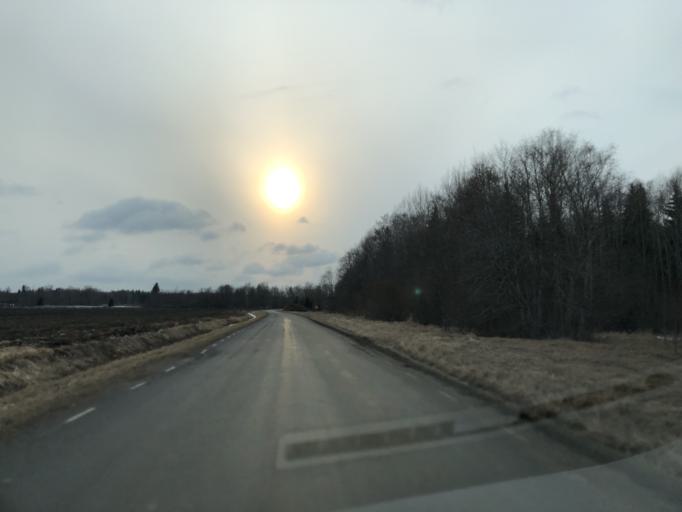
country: EE
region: Paernumaa
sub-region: Vaendra vald (alev)
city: Vandra
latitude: 58.6943
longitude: 24.9449
